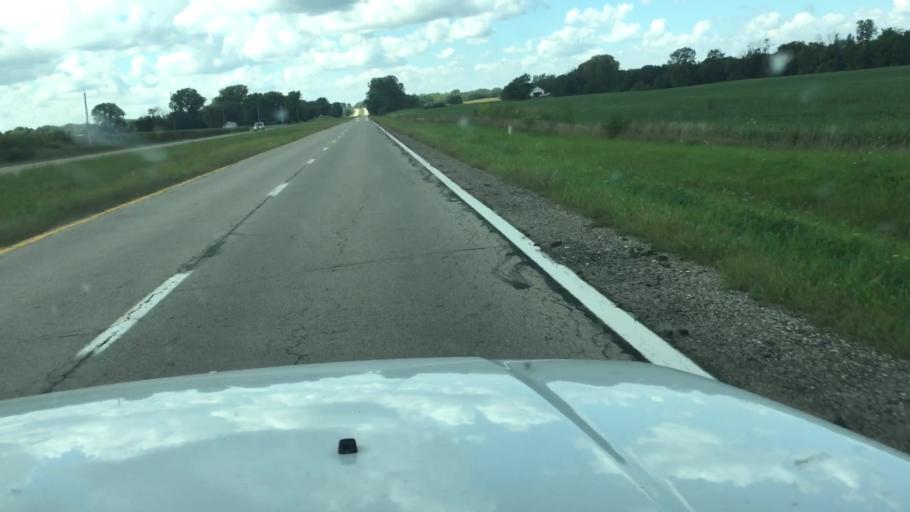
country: US
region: Ohio
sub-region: Madison County
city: Choctaw Lake
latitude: 39.9331
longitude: -83.5057
